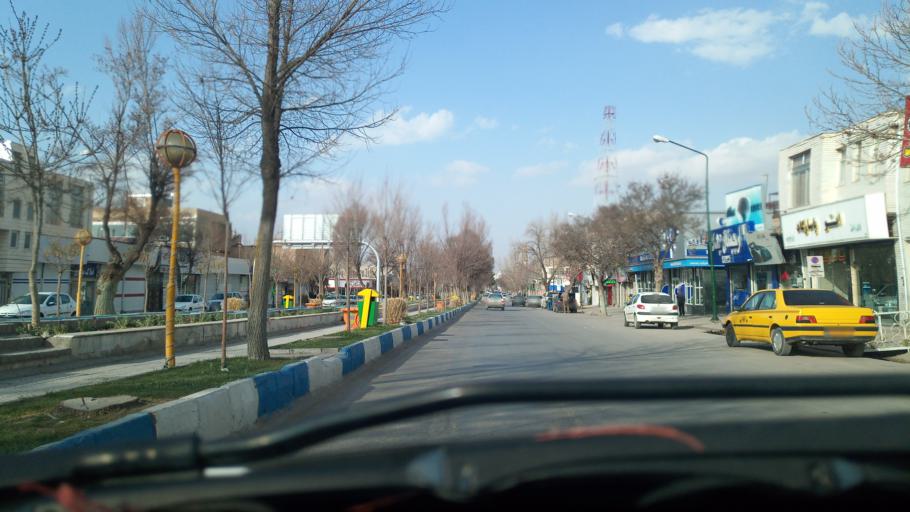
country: IR
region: Razavi Khorasan
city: Quchan
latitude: 37.0977
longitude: 58.5027
